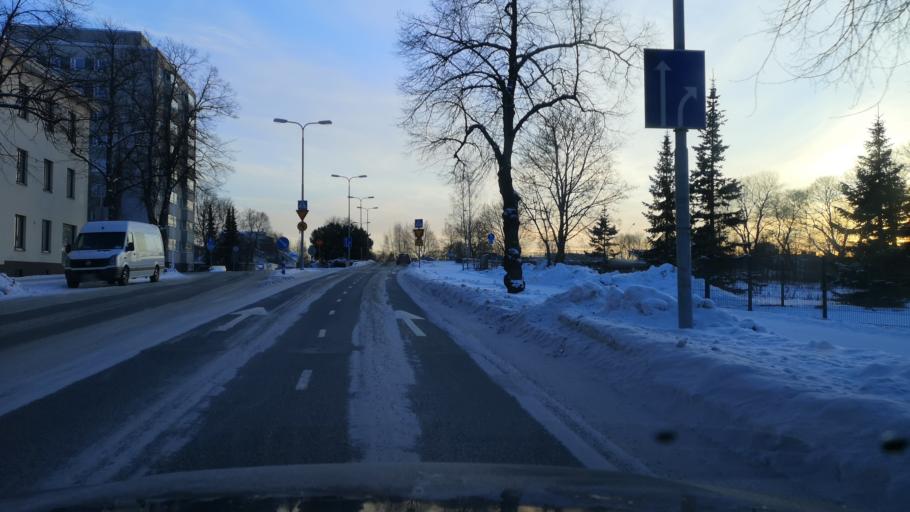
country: FI
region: Satakunta
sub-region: Pori
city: Pori
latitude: 61.4850
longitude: 21.7829
